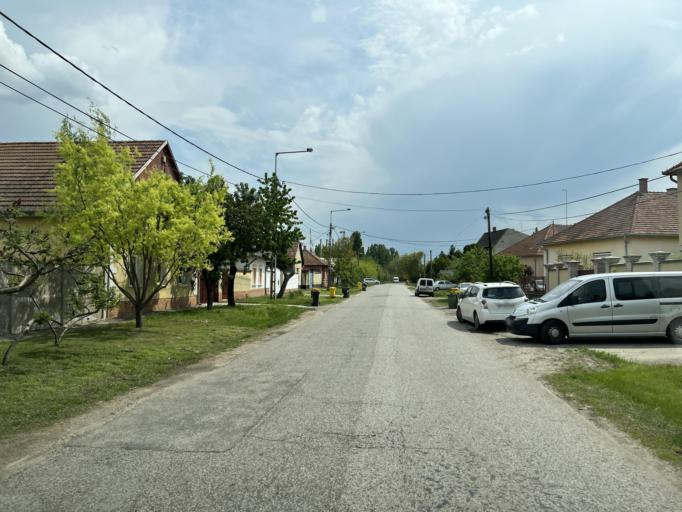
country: HU
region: Pest
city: Nagykoros
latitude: 47.0233
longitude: 19.7893
